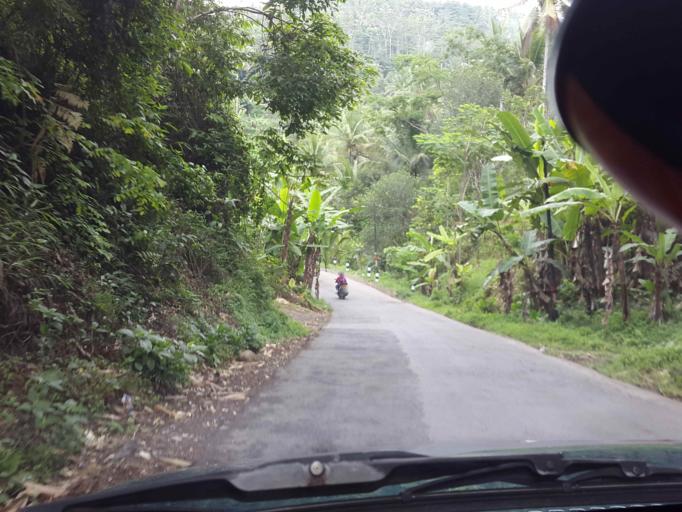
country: ID
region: Central Java
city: Magelang
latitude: -7.5204
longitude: 110.0553
